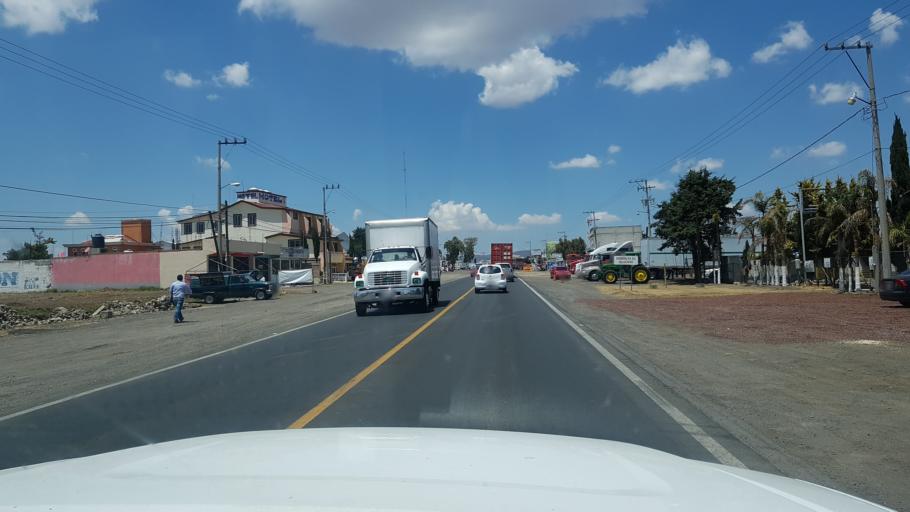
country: MX
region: Hidalgo
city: Calpulalpan
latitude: 19.5907
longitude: -98.5579
